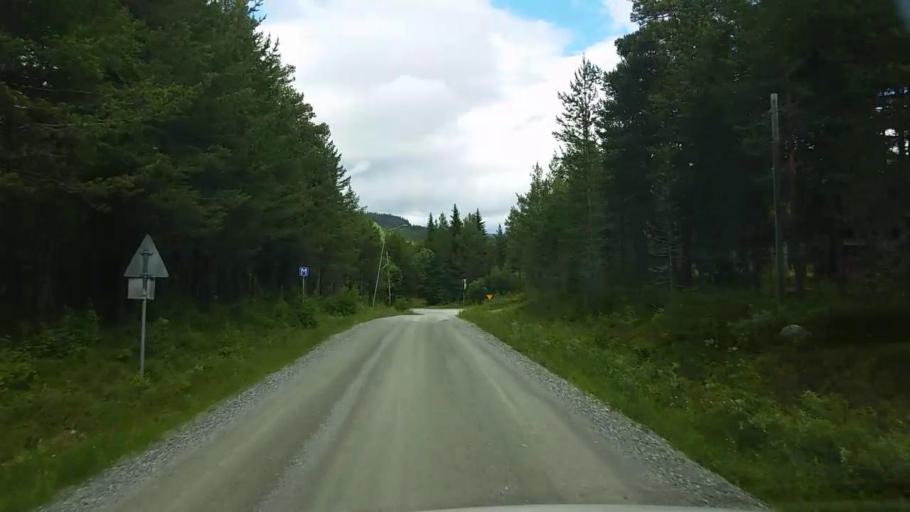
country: NO
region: Hedmark
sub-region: Engerdal
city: Engerdal
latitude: 62.4266
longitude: 12.6817
